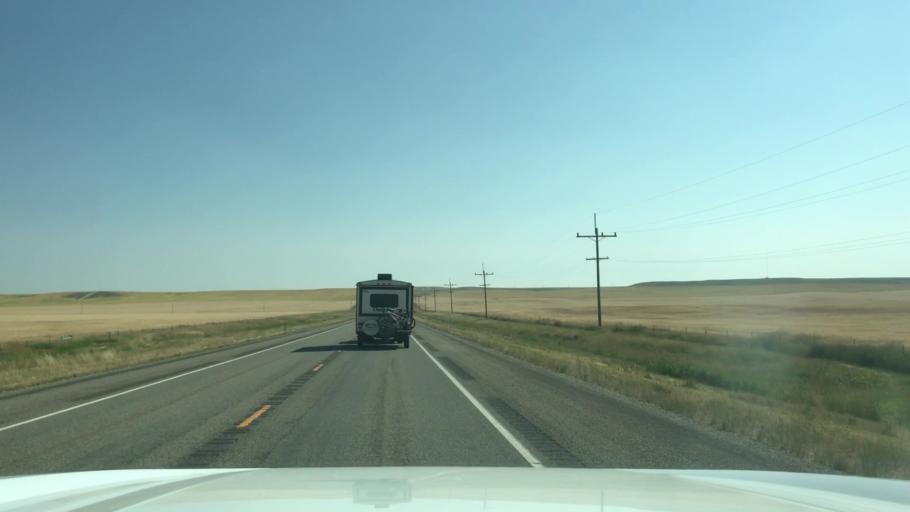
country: US
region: Montana
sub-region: Wheatland County
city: Harlowton
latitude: 46.4863
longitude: -109.7661
